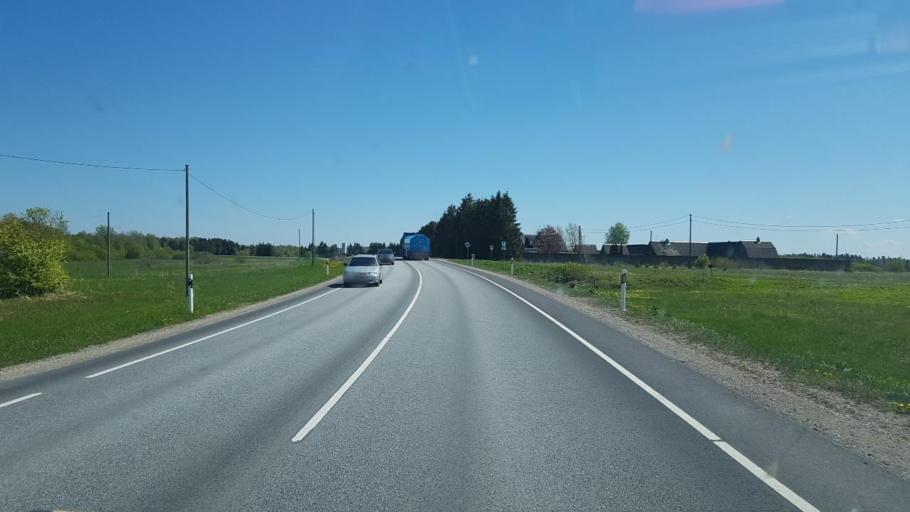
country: EE
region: Ida-Virumaa
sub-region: Narva-Joesuu linn
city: Narva-Joesuu
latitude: 59.3747
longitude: 27.9392
